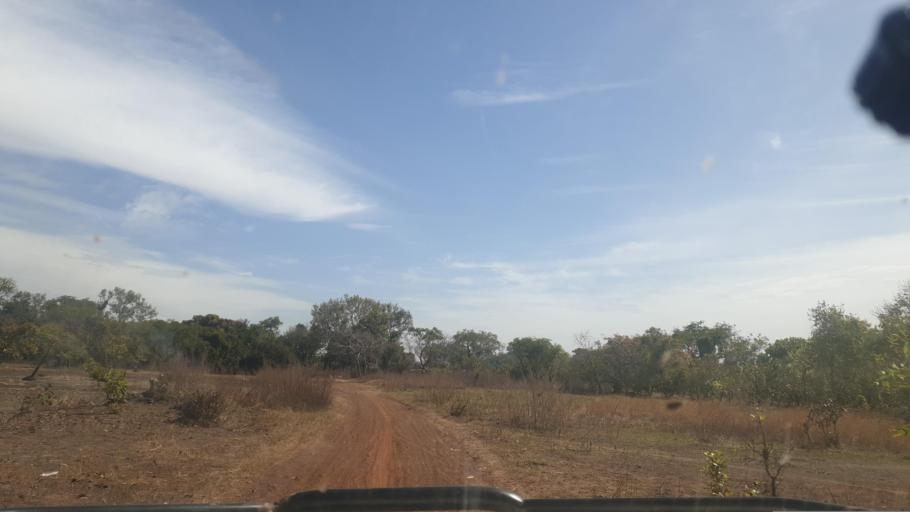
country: ML
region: Sikasso
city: Yanfolila
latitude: 10.4983
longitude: -7.9581
